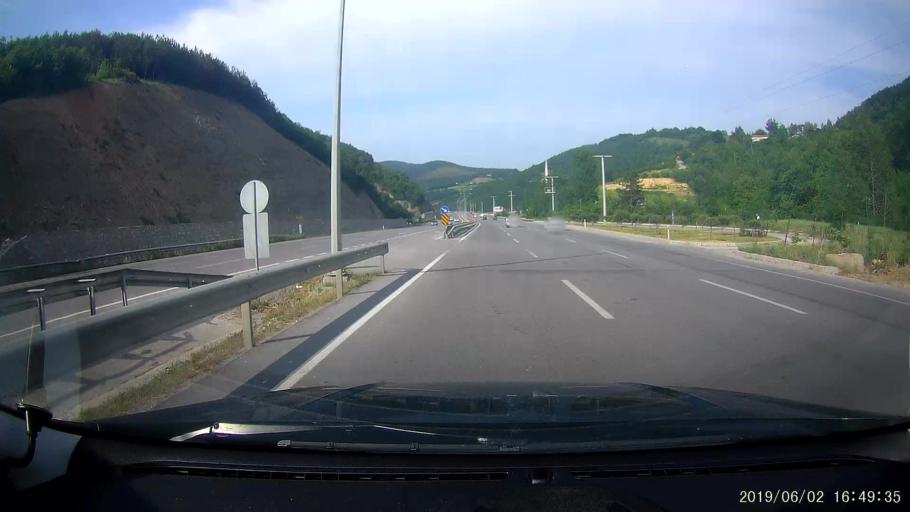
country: TR
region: Samsun
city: Samsun
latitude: 41.2397
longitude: 36.1651
